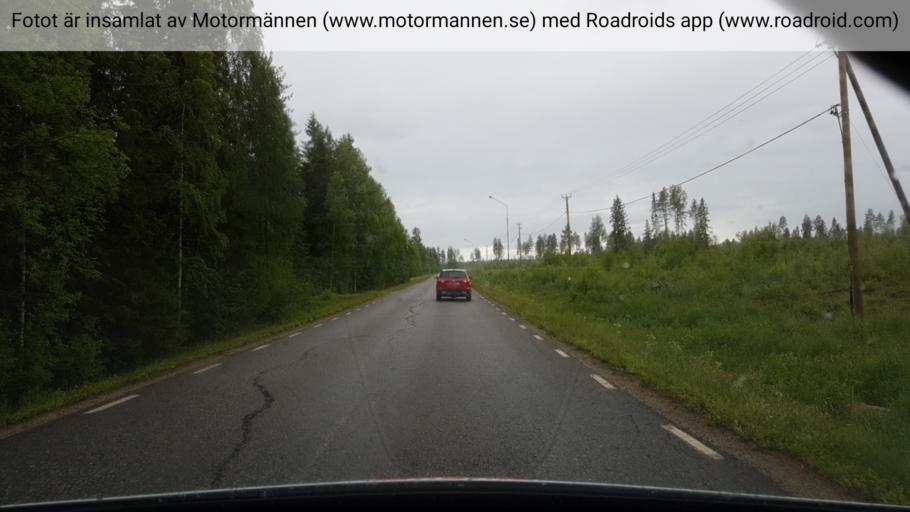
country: SE
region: Vaesterbotten
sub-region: Bjurholms Kommun
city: Bjurholm
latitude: 64.1419
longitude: 19.3119
